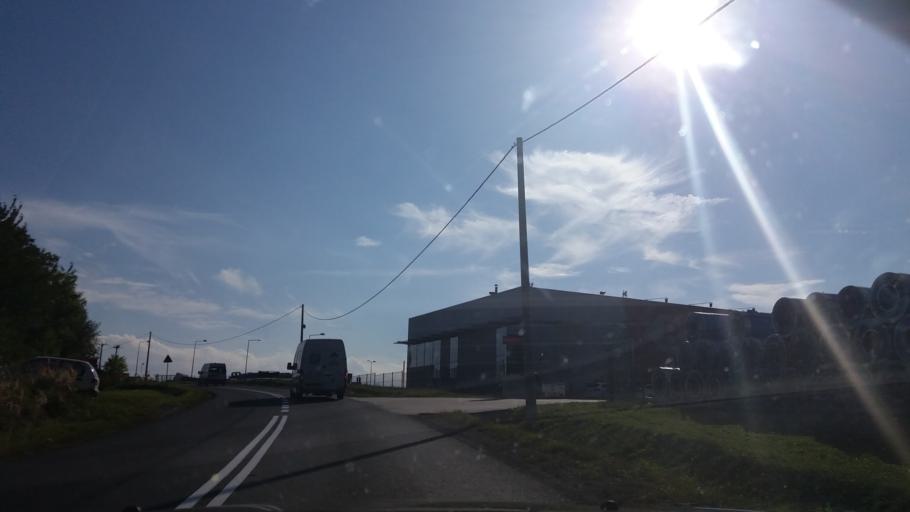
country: PL
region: Lesser Poland Voivodeship
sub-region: Powiat chrzanowski
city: Grojec
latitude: 50.0978
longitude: 19.5537
